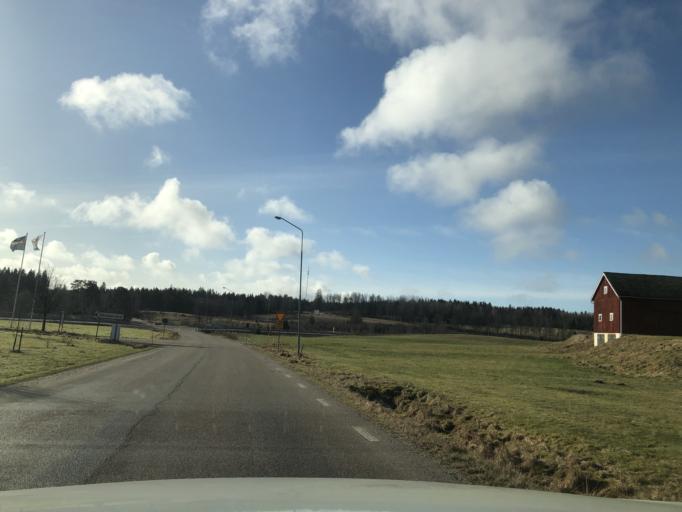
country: SE
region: Vaestra Goetaland
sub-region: Ulricehamns Kommun
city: Ulricehamn
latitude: 57.7988
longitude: 13.5955
